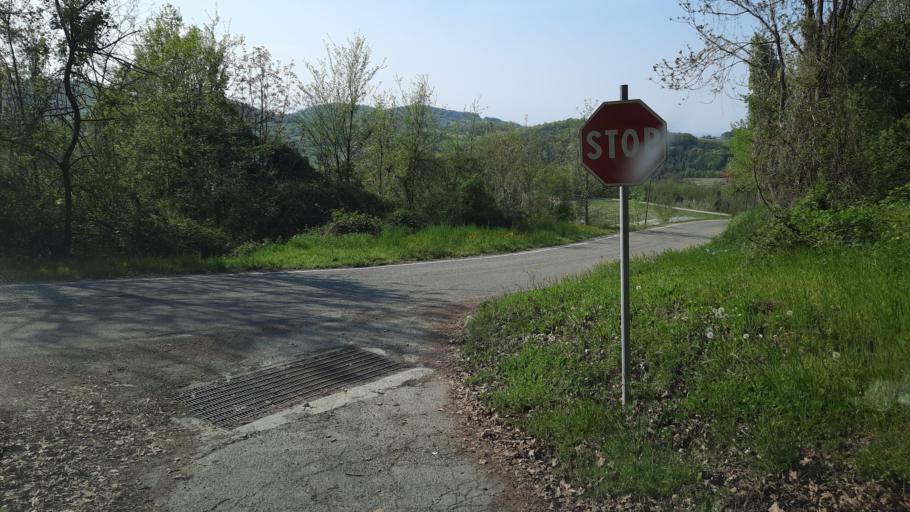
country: IT
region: Piedmont
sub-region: Provincia di Alessandria
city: Villamiroglio
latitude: 45.1370
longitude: 8.1718
